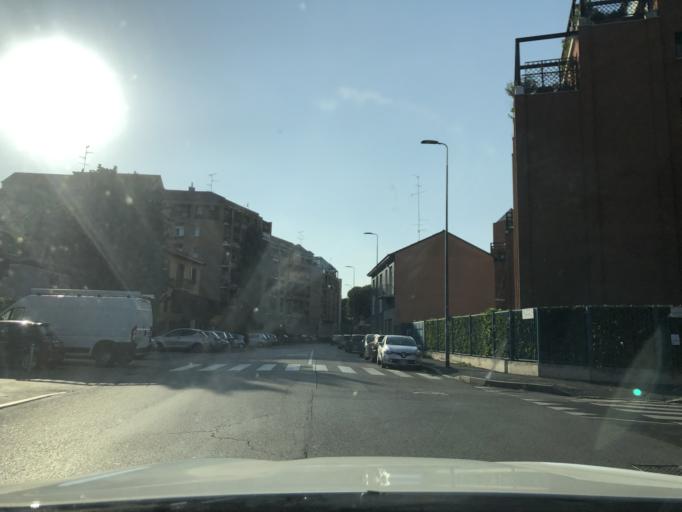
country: IT
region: Lombardy
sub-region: Citta metropolitana di Milano
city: Baranzate
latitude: 45.5046
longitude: 9.1255
